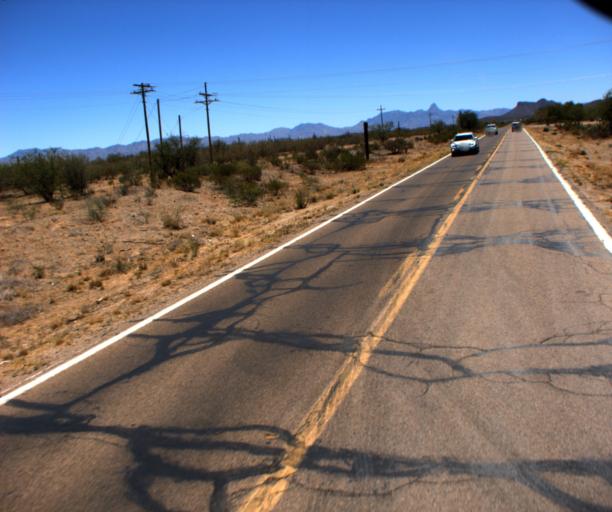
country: US
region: Arizona
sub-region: Pima County
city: Sells
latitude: 31.9355
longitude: -111.9145
